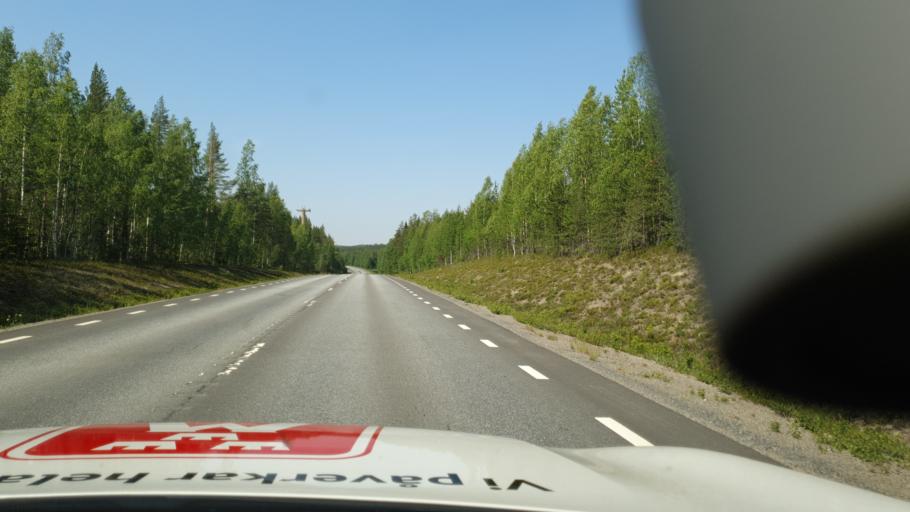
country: SE
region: Vaesterbotten
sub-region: Norsjo Kommun
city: Norsjoe
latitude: 64.9711
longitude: 19.7543
